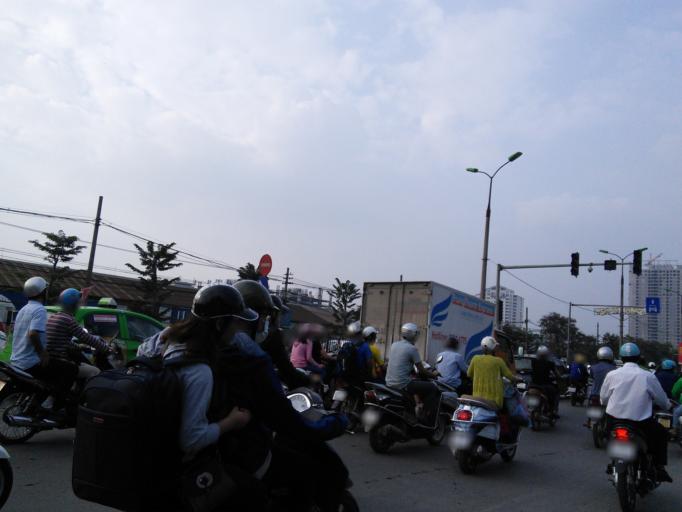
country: VN
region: Ha Noi
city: Van Dien
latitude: 20.9795
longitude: 105.8411
